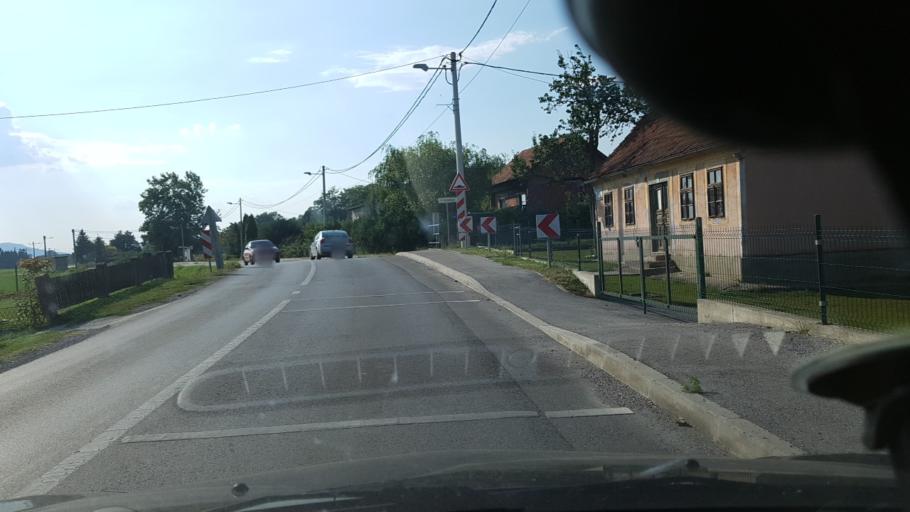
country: HR
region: Zagrebacka
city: Bregana
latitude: 45.8842
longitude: 15.7131
